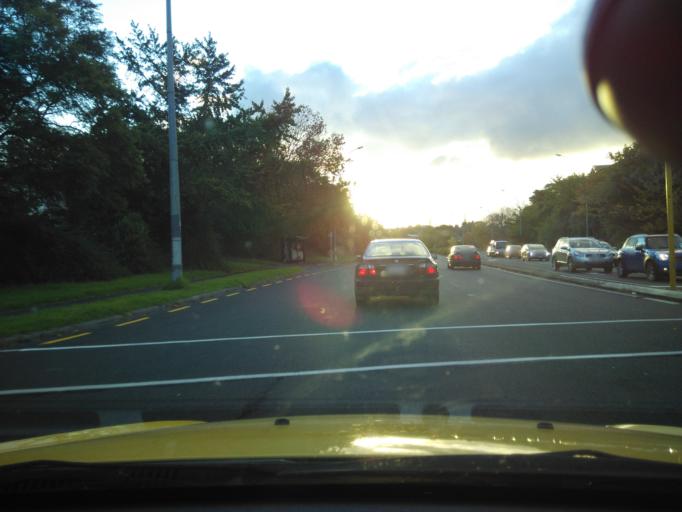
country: NZ
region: Auckland
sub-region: Auckland
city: Auckland
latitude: -36.8926
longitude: 174.7701
